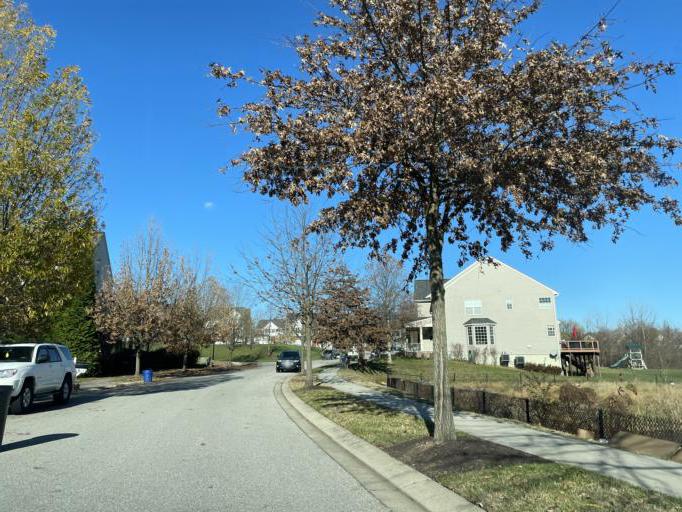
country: US
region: Maryland
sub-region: Baltimore County
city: Pikesville
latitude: 39.3729
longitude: -76.6696
